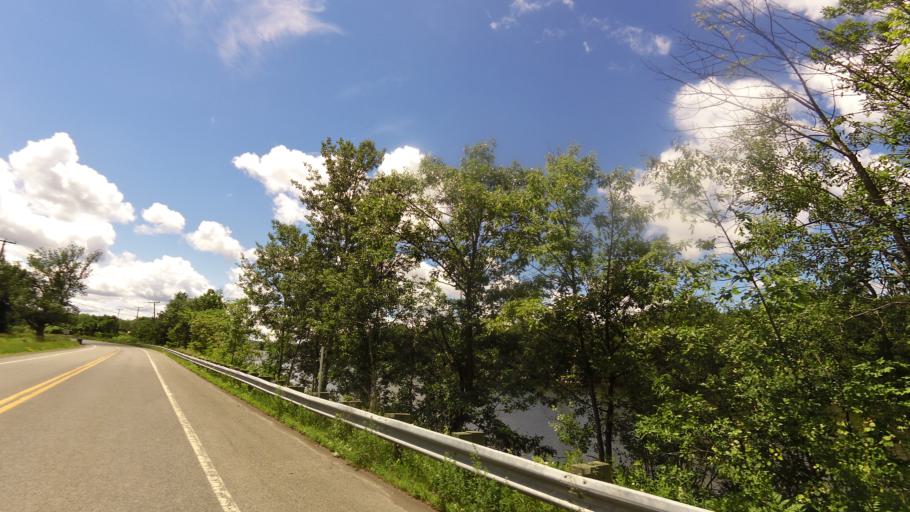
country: CA
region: Quebec
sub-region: Monteregie
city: Rigaud
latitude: 45.5411
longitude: -74.3331
